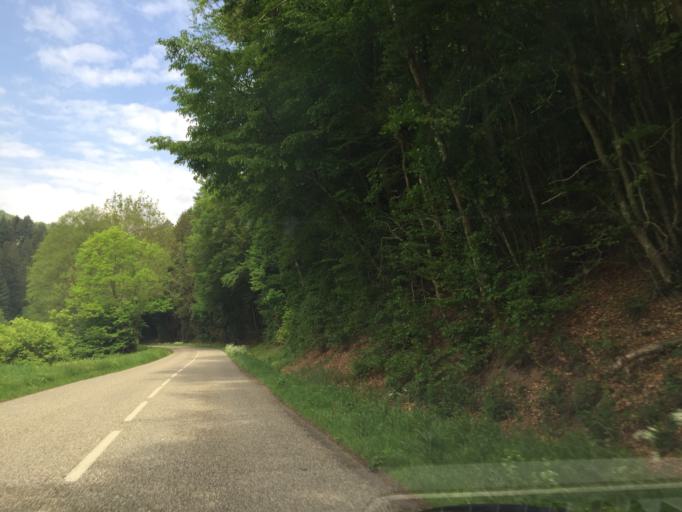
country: FR
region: Alsace
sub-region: Departement du Bas-Rhin
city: Lembach
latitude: 49.0211
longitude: 7.7731
